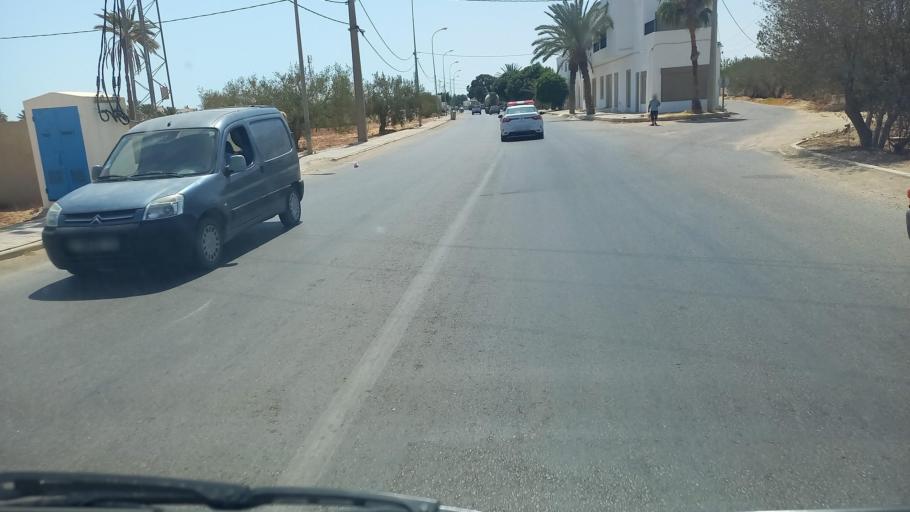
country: TN
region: Madanin
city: Houmt Souk
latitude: 33.7781
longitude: 10.8925
